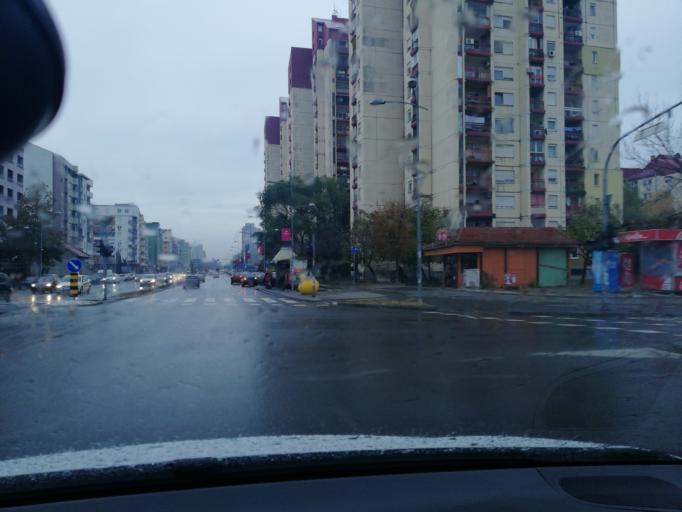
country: RS
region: Autonomna Pokrajina Vojvodina
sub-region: Juznobacki Okrug
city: Novi Sad
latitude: 45.2398
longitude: 19.8252
